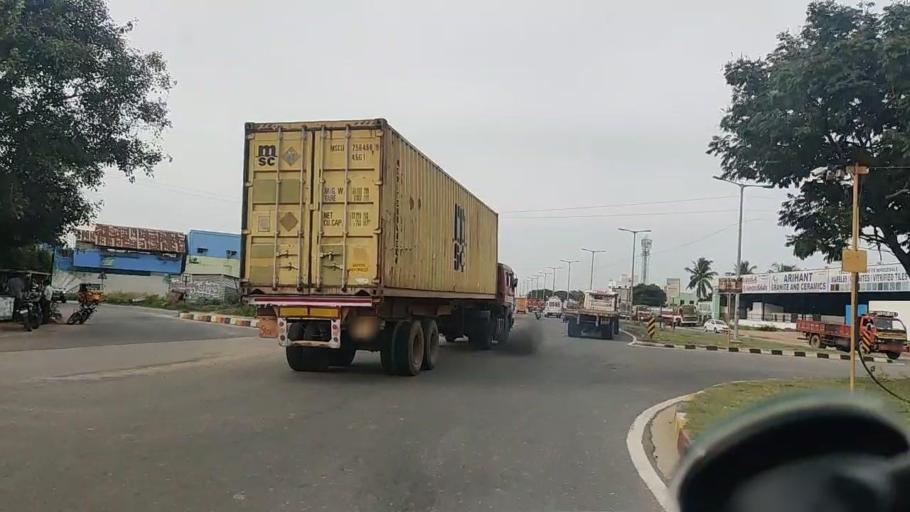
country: IN
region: Tamil Nadu
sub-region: Thiruvallur
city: Chinnasekkadu
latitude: 13.1584
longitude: 80.2257
